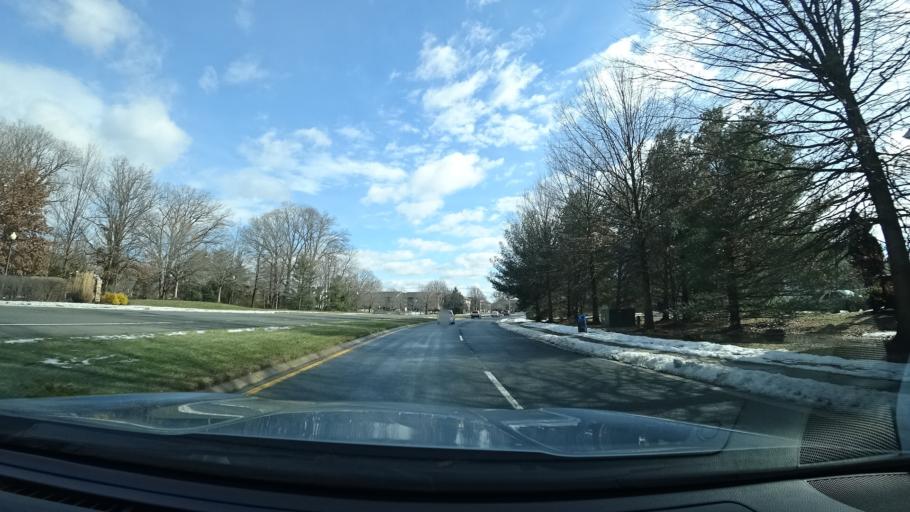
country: US
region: Virginia
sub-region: Loudoun County
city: Sugarland Run
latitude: 39.0358
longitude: -77.3889
